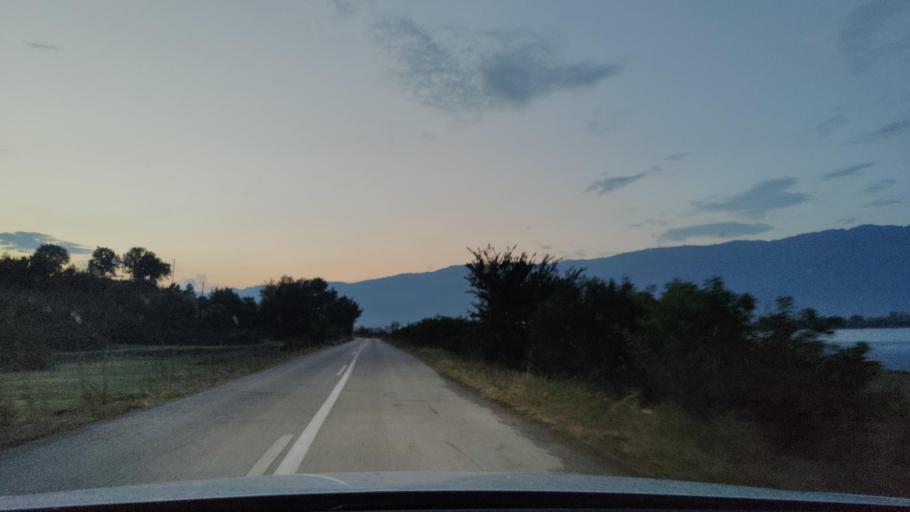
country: GR
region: Central Macedonia
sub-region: Nomos Serron
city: Chrysochorafa
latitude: 41.1960
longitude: 23.0926
